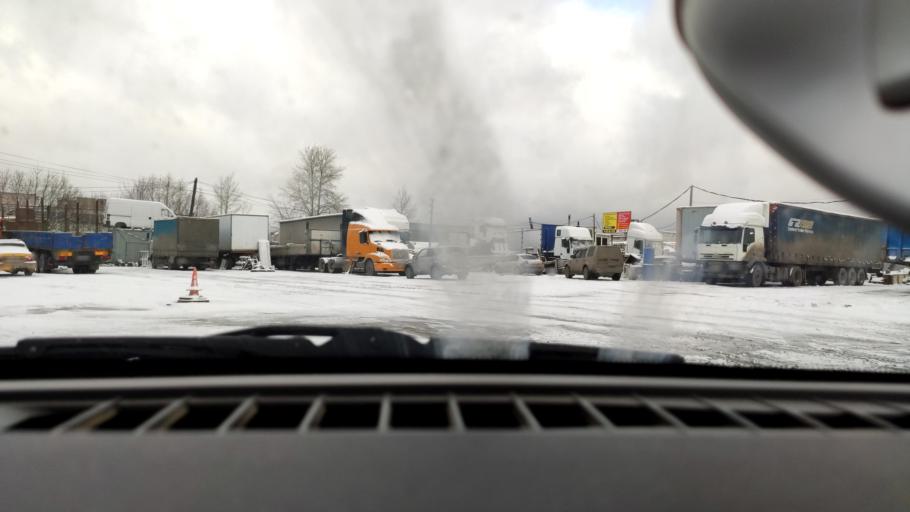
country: RU
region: Perm
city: Froly
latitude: 57.9703
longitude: 56.2888
